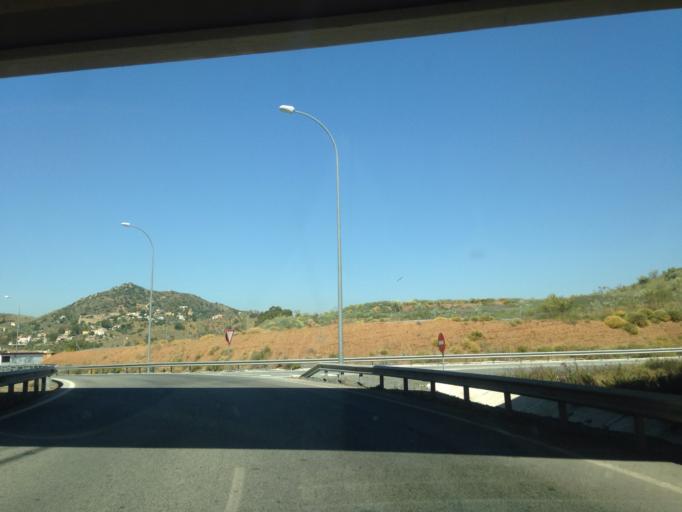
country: ES
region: Andalusia
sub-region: Provincia de Malaga
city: Malaga
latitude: 36.7521
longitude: -4.4915
